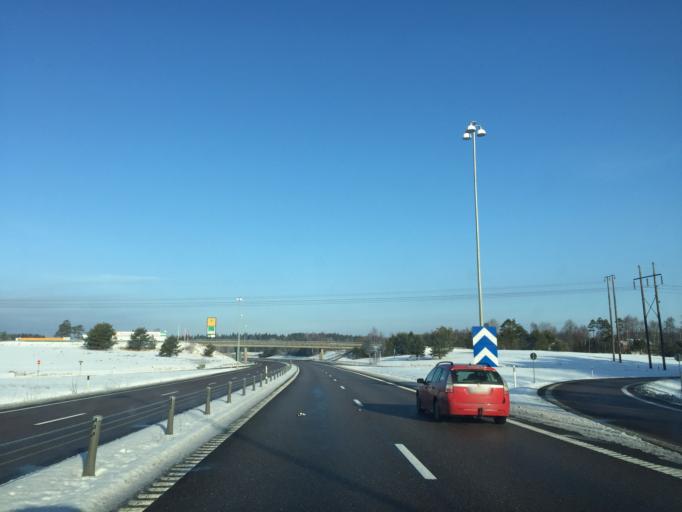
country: SE
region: Vaestra Goetaland
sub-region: Tanums Kommun
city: Tanumshede
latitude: 58.7180
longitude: 11.3538
